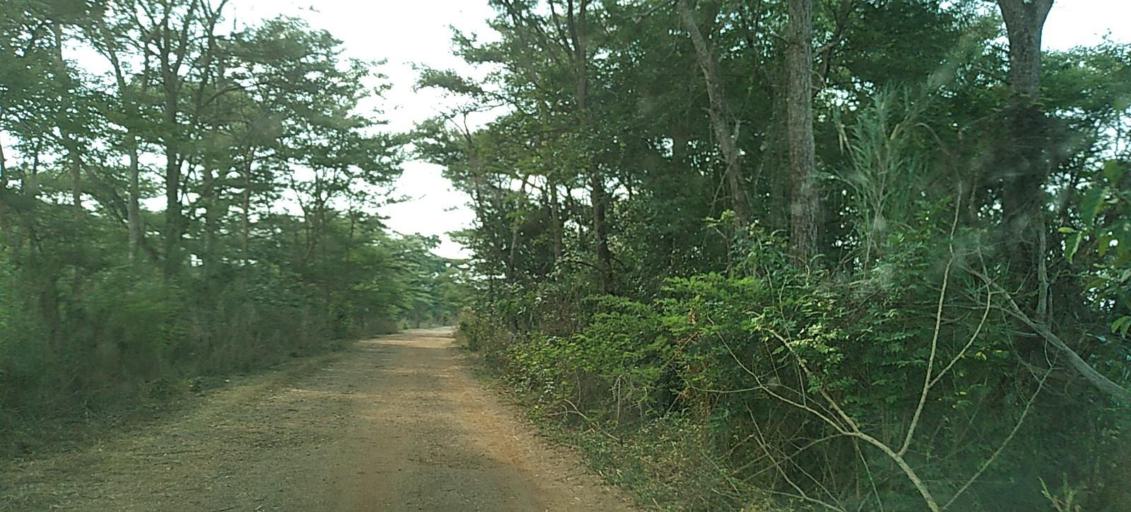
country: ZM
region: Copperbelt
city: Mpongwe
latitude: -13.4754
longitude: 28.0770
